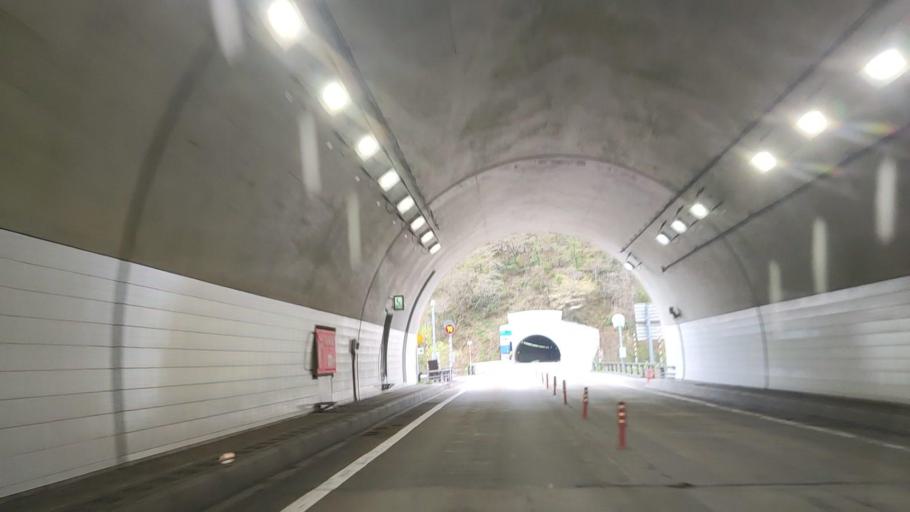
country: JP
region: Akita
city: Odate
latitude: 40.3568
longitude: 140.6904
